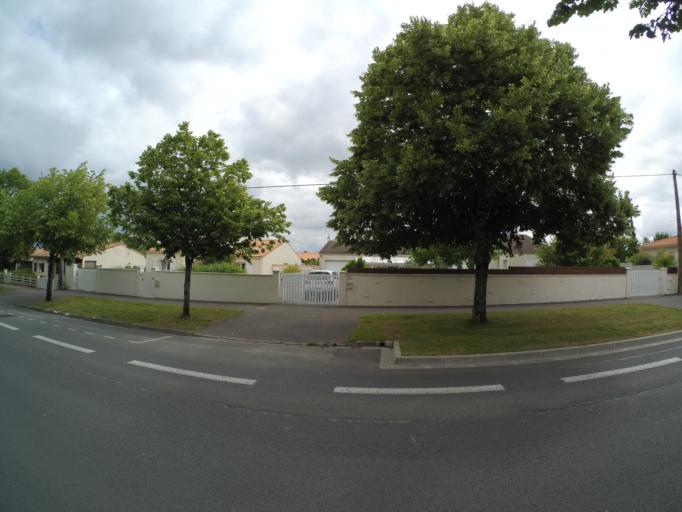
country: FR
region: Poitou-Charentes
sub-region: Departement de la Charente-Maritime
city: Rochefort
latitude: 45.9543
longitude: -0.9690
